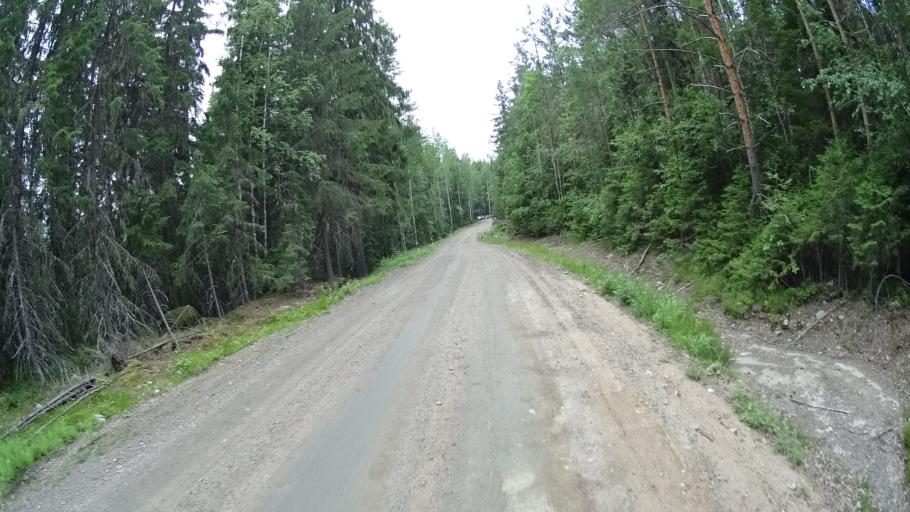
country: FI
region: Southern Savonia
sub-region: Mikkeli
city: Maentyharju
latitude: 61.1544
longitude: 26.8892
